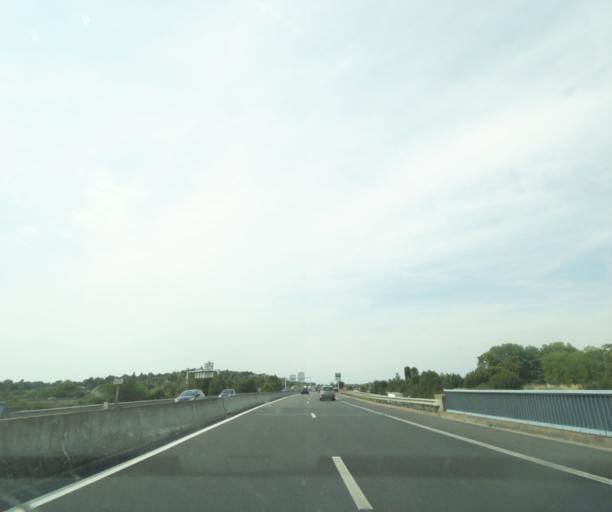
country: FR
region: Centre
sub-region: Departement d'Indre-et-Loire
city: Saint-Cyr-sur-Loire
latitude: 47.3873
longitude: 0.6494
